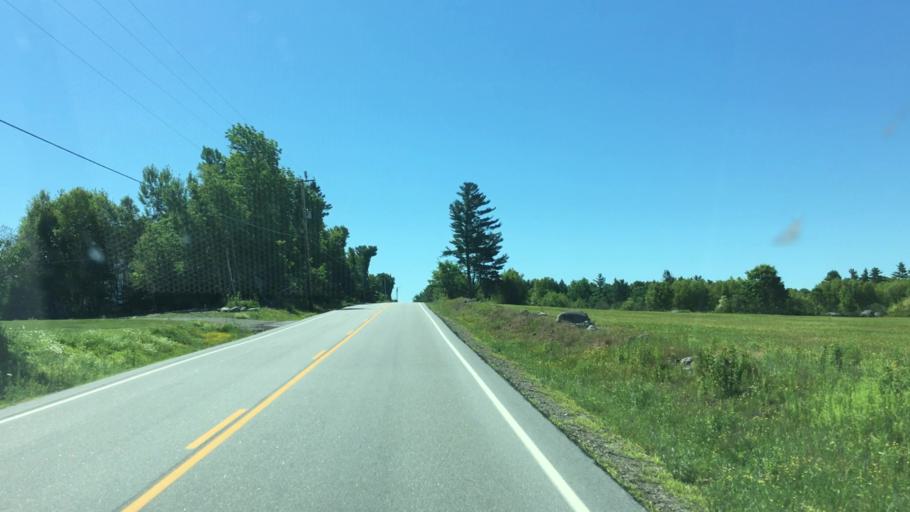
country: US
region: Maine
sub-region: Hancock County
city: Orland
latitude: 44.5488
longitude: -68.6905
